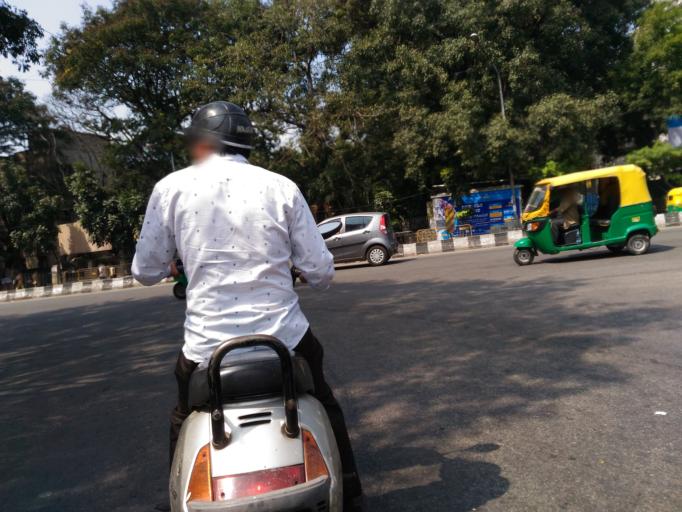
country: IN
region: Karnataka
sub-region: Bangalore Urban
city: Bangalore
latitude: 12.9636
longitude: 77.5849
